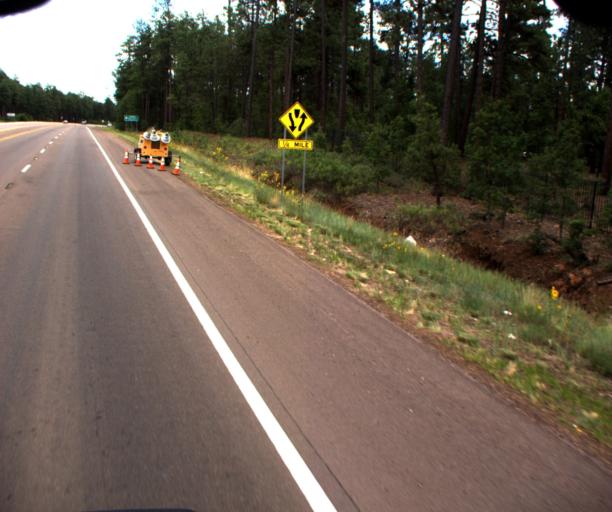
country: US
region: Arizona
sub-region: Navajo County
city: Pinetop-Lakeside
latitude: 34.1233
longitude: -109.9235
